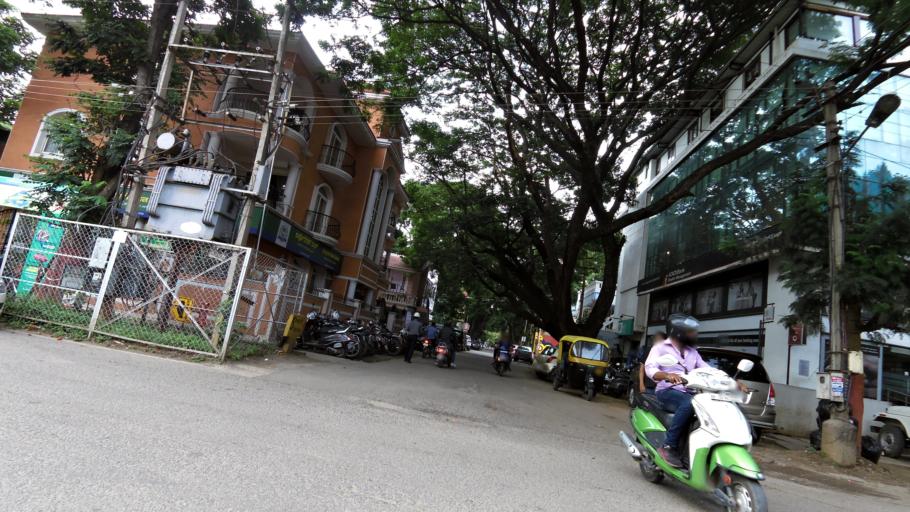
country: IN
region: Karnataka
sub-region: Bangalore Urban
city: Bangalore
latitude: 12.9700
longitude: 77.6388
